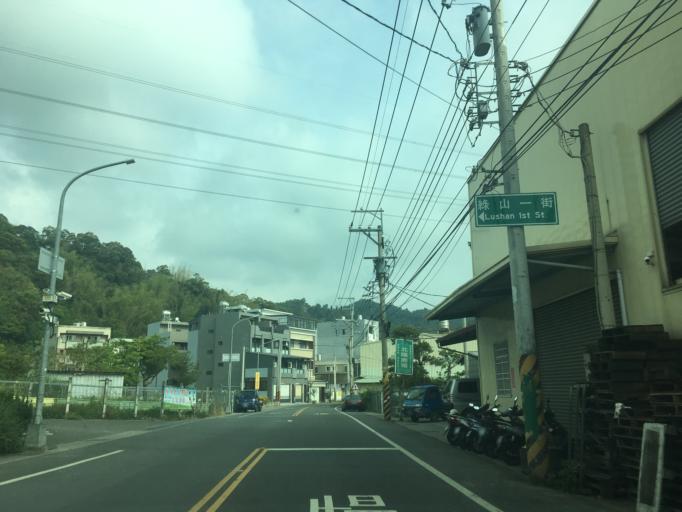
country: TW
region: Taiwan
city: Fengyuan
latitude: 24.2402
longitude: 120.7334
